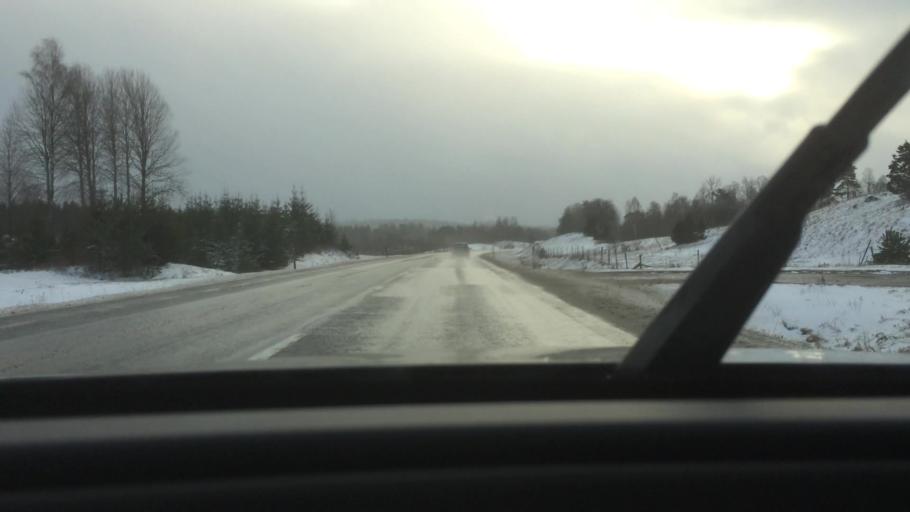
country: SE
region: Vaestra Goetaland
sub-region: Falkopings Kommun
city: Falkoeping
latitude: 57.9755
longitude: 13.5286
